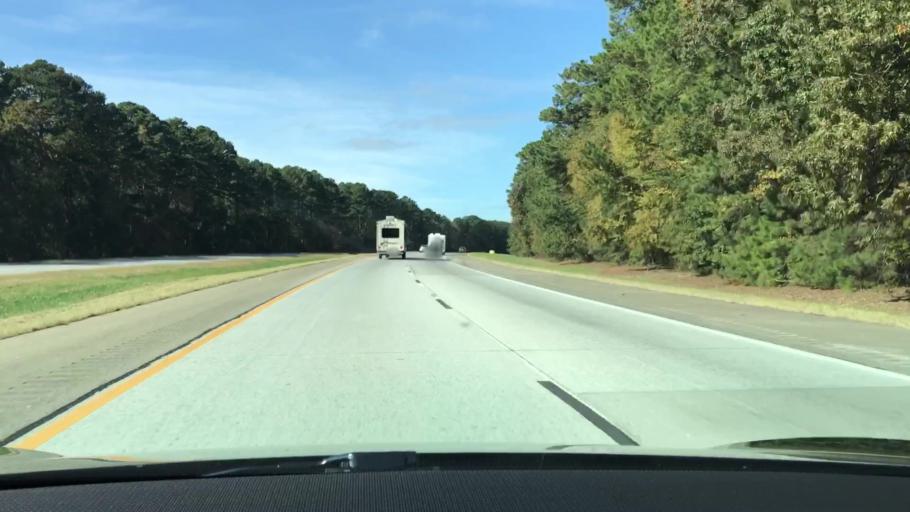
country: US
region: Georgia
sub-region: Putnam County
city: Jefferson
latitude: 33.5330
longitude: -83.2894
